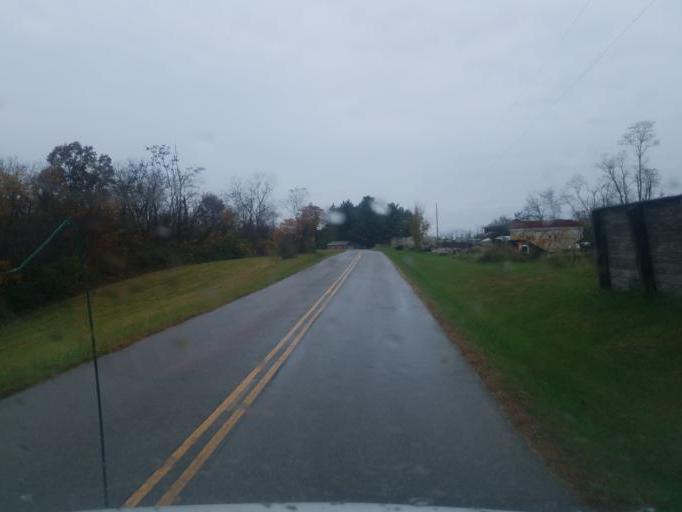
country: US
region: Ohio
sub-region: Washington County
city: Beverly
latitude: 39.4437
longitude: -81.6224
